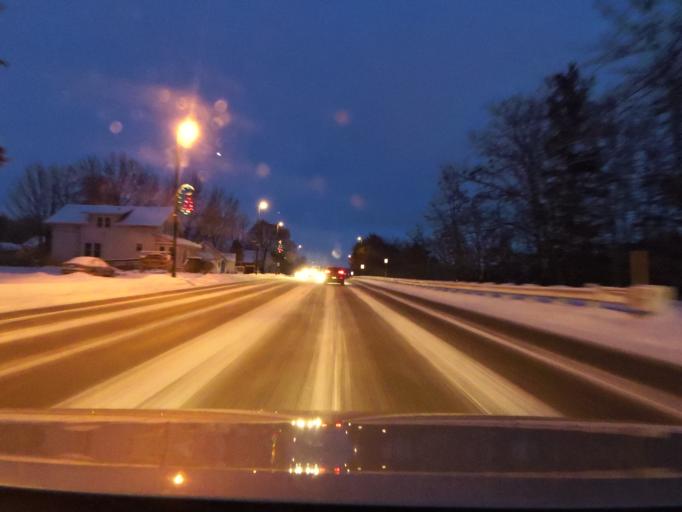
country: US
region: Wisconsin
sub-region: Dunn County
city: Menomonie
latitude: 44.8914
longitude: -91.9320
